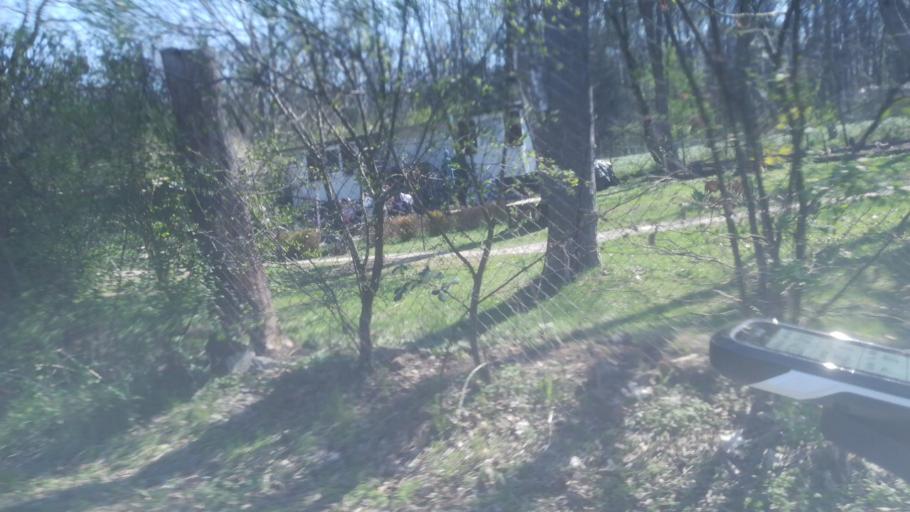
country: DE
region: Baden-Wuerttemberg
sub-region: Freiburg Region
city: Singen
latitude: 47.7811
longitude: 8.8426
